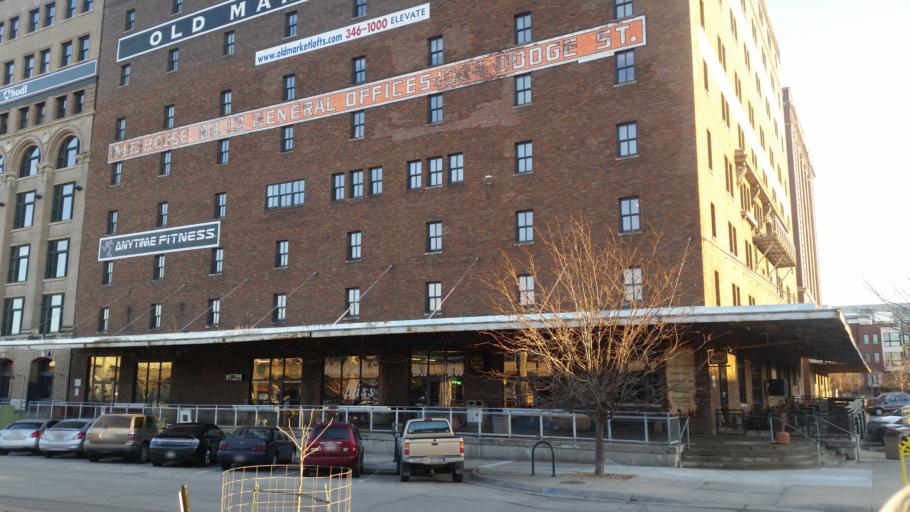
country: US
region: Nebraska
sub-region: Douglas County
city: Omaha
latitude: 41.2535
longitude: -95.9306
